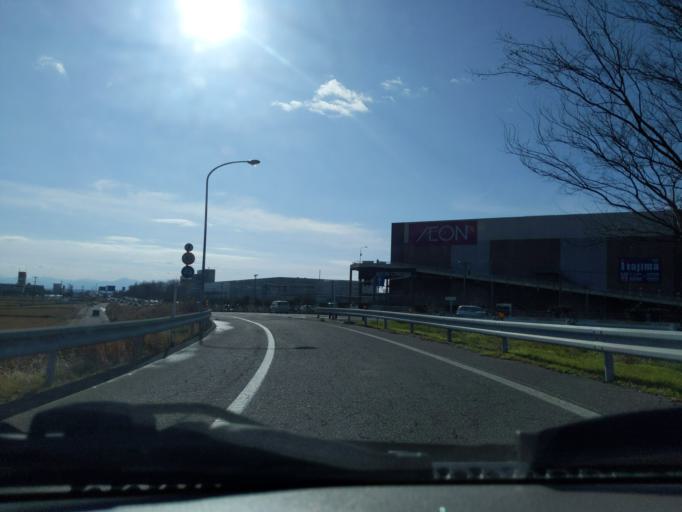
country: JP
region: Niigata
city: Kameda-honcho
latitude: 37.8784
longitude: 139.0834
